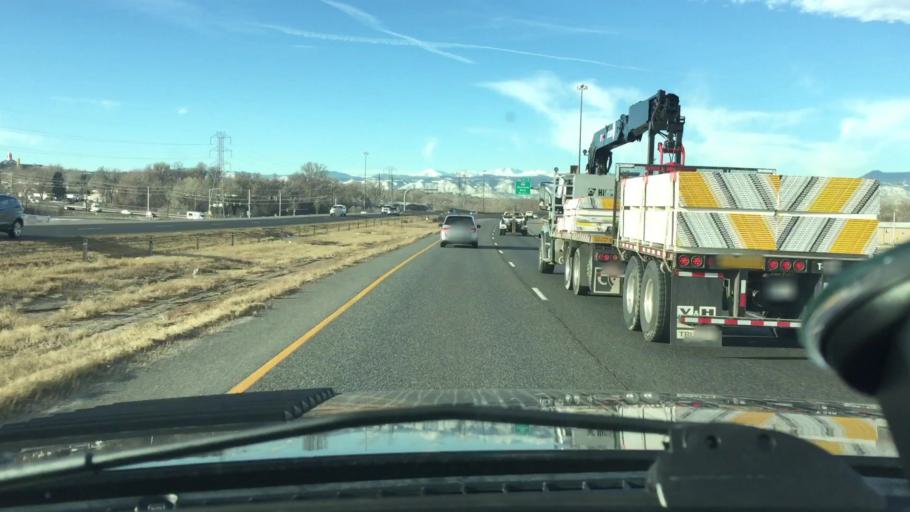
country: US
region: Colorado
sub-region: Adams County
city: Berkley
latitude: 39.8016
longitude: -105.0224
